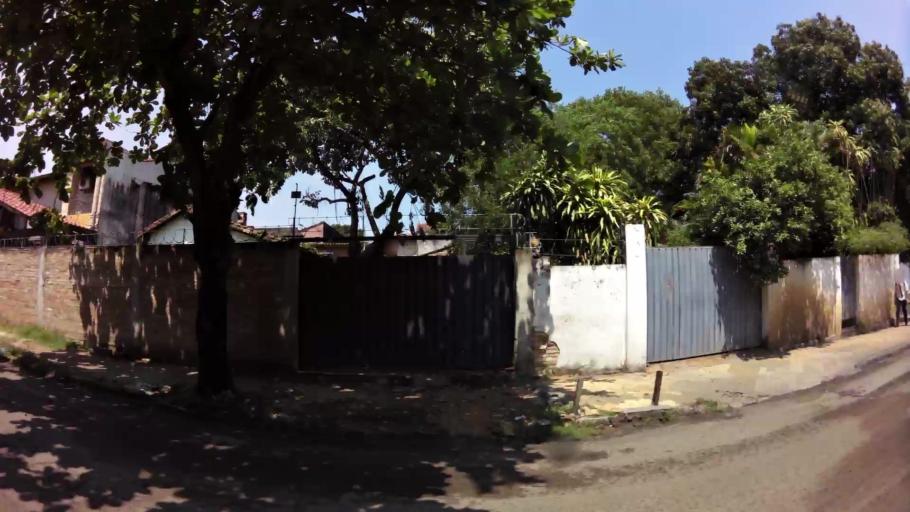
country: PY
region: Asuncion
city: Asuncion
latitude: -25.3015
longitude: -57.6383
